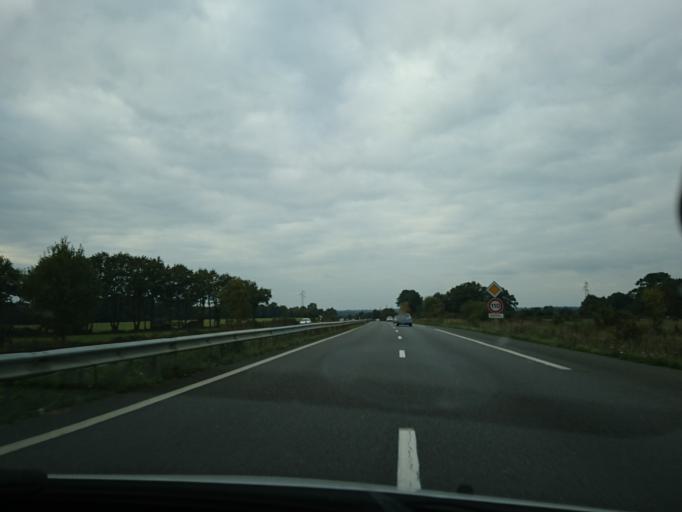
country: FR
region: Pays de la Loire
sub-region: Departement de la Loire-Atlantique
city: Pontchateau
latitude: 47.4278
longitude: -2.0602
